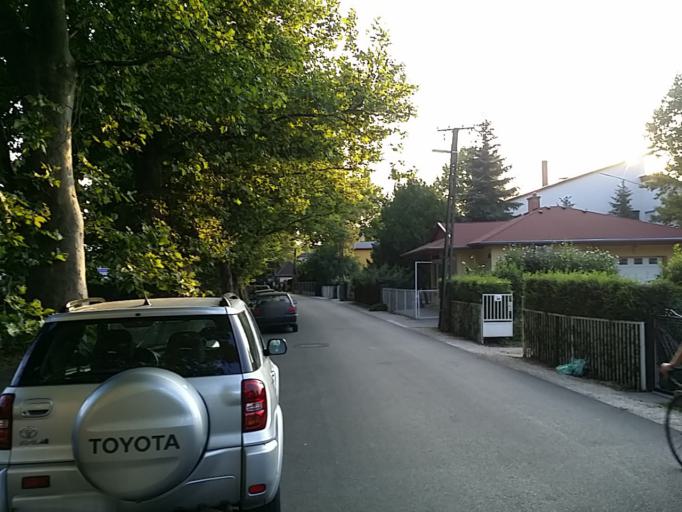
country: HU
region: Somogy
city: Balatonboglar
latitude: 46.7830
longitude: 17.6634
